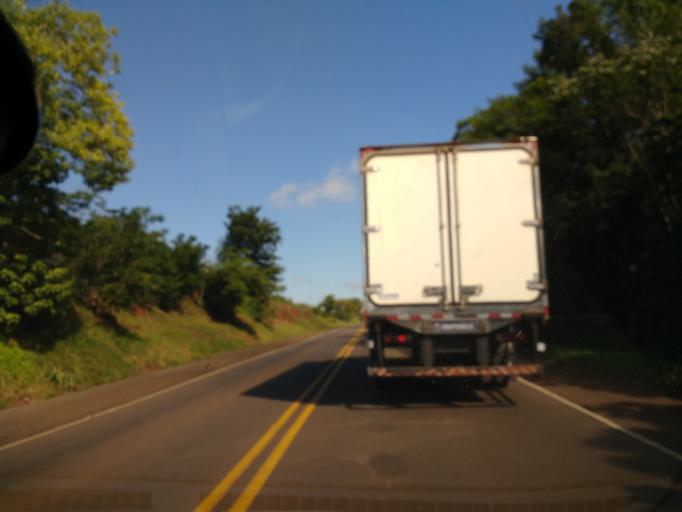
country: BR
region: Parana
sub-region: Terra Boa
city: Terra Boa
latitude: -23.5987
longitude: -52.3943
